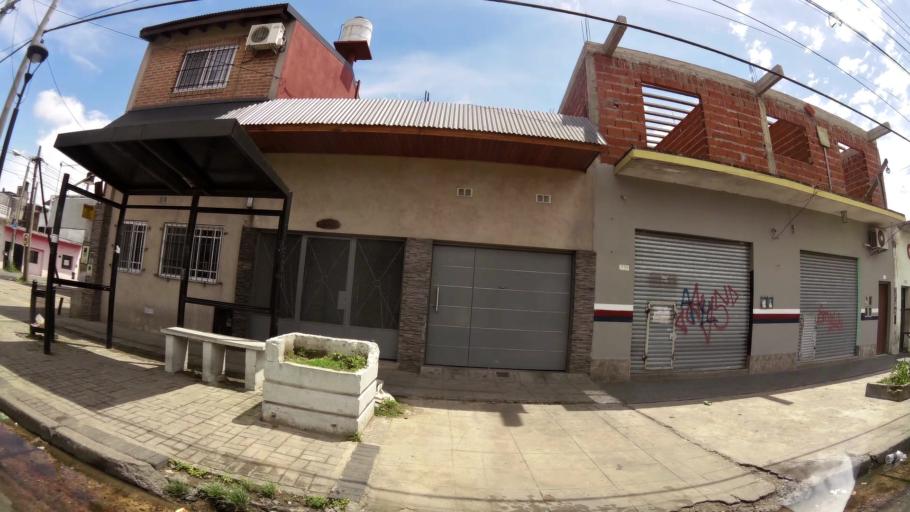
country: AR
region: Buenos Aires
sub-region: Partido de Quilmes
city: Quilmes
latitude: -34.7760
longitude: -58.2537
